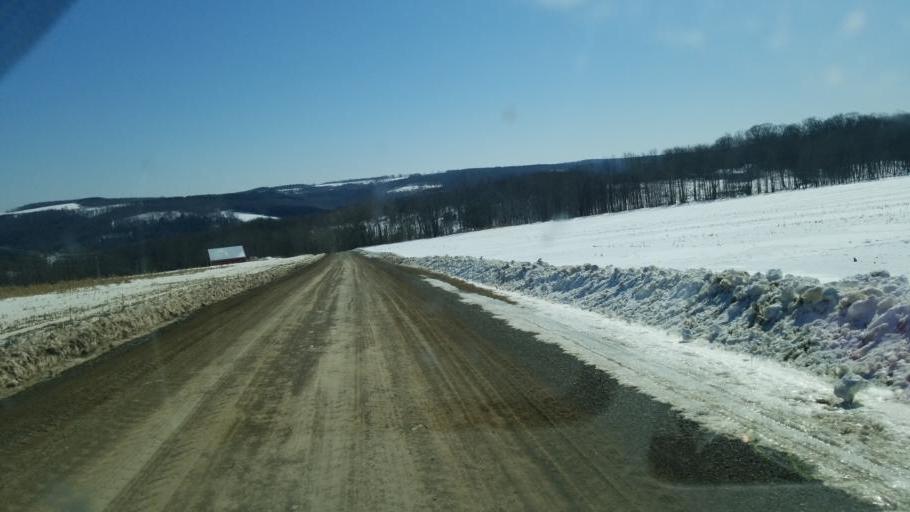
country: US
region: New York
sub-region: Allegany County
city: Andover
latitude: 42.0922
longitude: -77.6760
